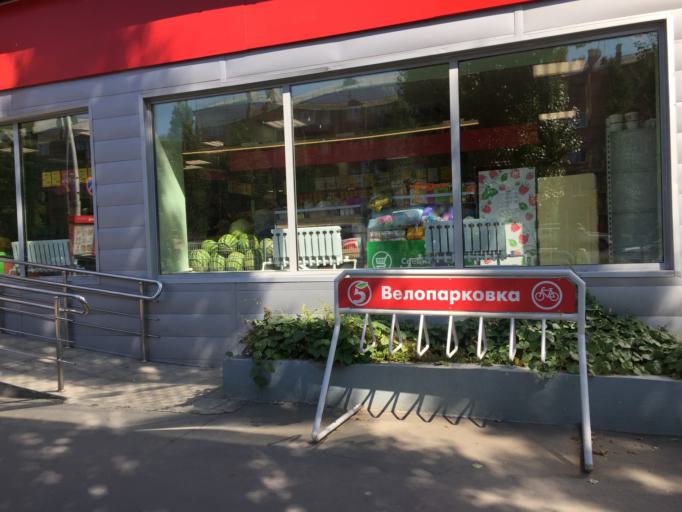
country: RU
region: Orenburg
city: Novotroitsk
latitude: 51.1964
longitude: 58.3057
